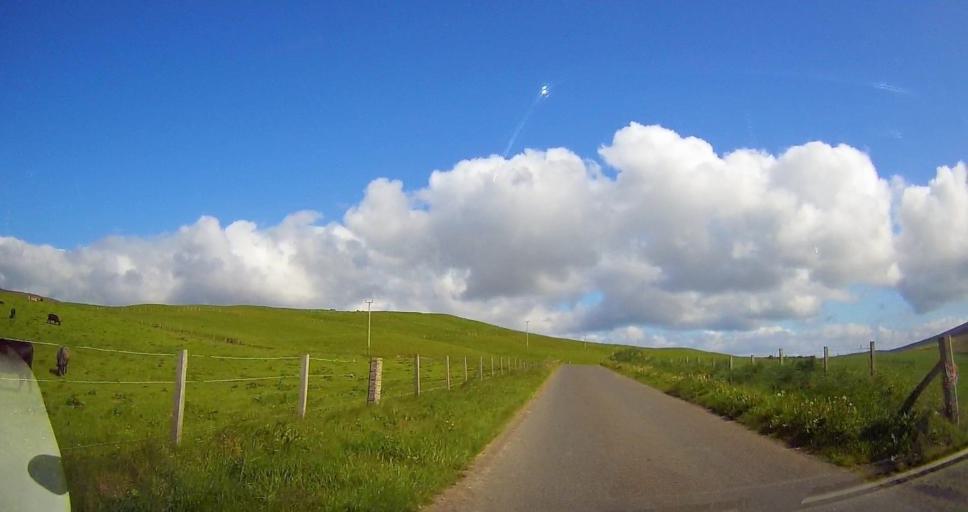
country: GB
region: Scotland
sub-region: Orkney Islands
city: Stromness
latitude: 58.9812
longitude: -3.1382
